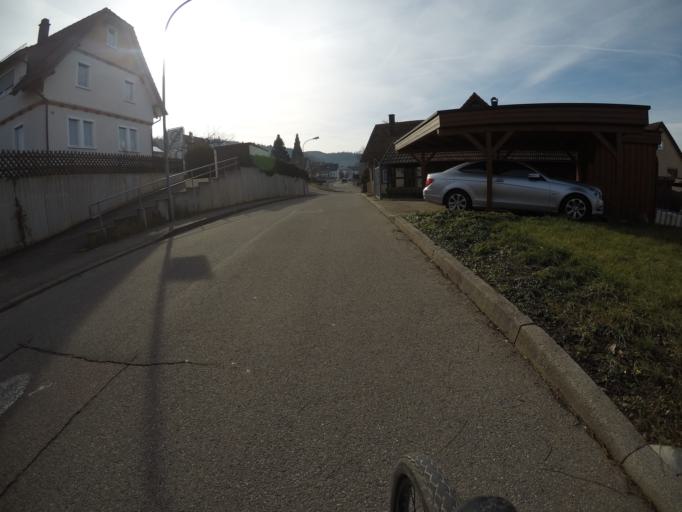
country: DE
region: Baden-Wuerttemberg
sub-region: Karlsruhe Region
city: Calw
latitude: 48.6915
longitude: 8.7708
